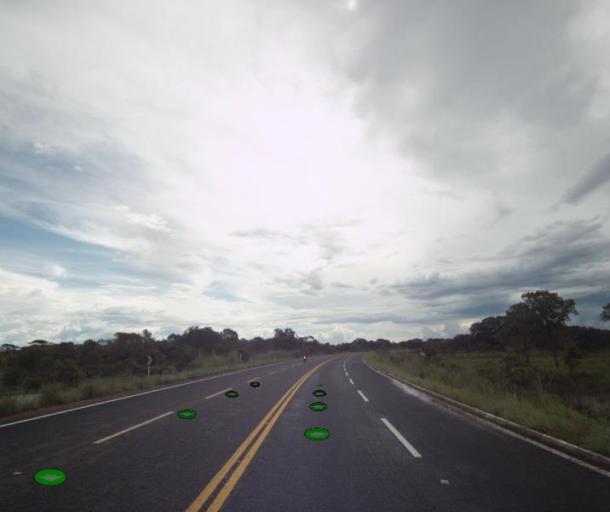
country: BR
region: Goias
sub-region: Sao Miguel Do Araguaia
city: Sao Miguel do Araguaia
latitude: -13.2340
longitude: -50.5621
